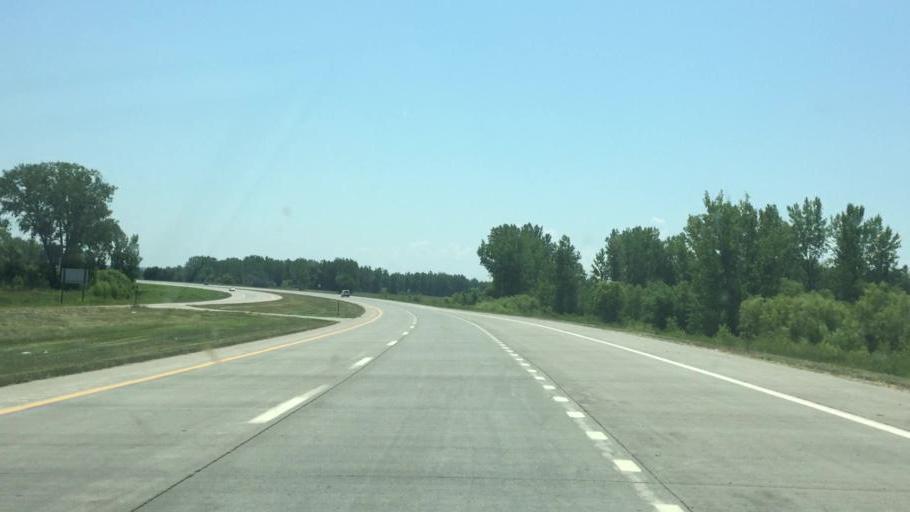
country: US
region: Kansas
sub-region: Doniphan County
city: Wathena
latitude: 39.7439
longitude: -94.9217
